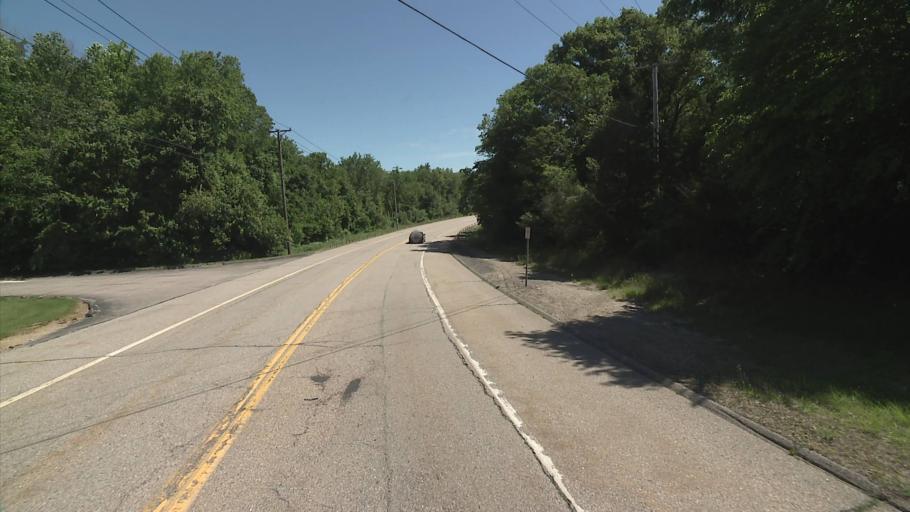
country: US
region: Connecticut
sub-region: New London County
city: Pawcatuck
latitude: 41.4166
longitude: -71.8537
